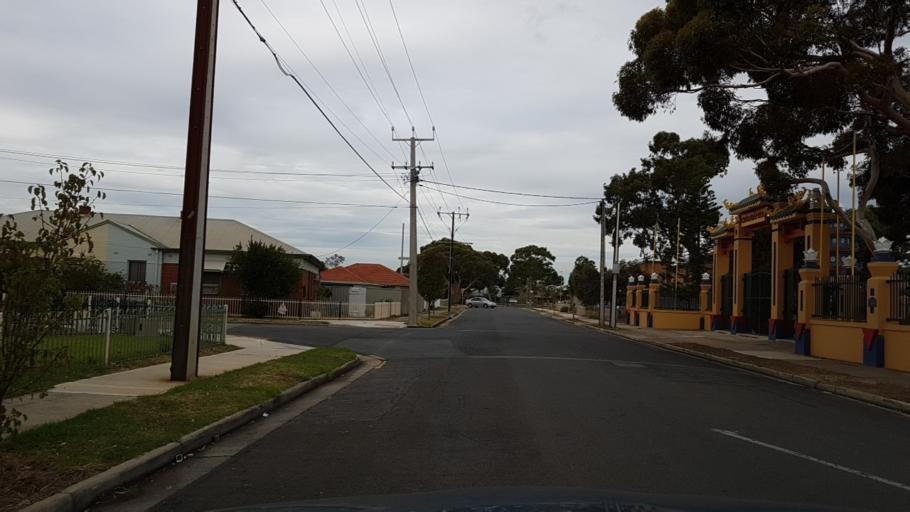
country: AU
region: South Australia
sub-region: Port Adelaide Enfield
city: Alberton
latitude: -34.8568
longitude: 138.5331
